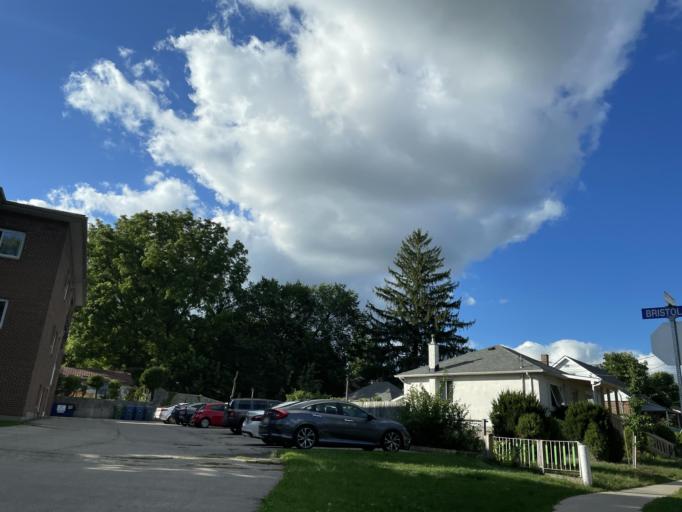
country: CA
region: Ontario
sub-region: Wellington County
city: Guelph
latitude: 43.5374
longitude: -80.2512
